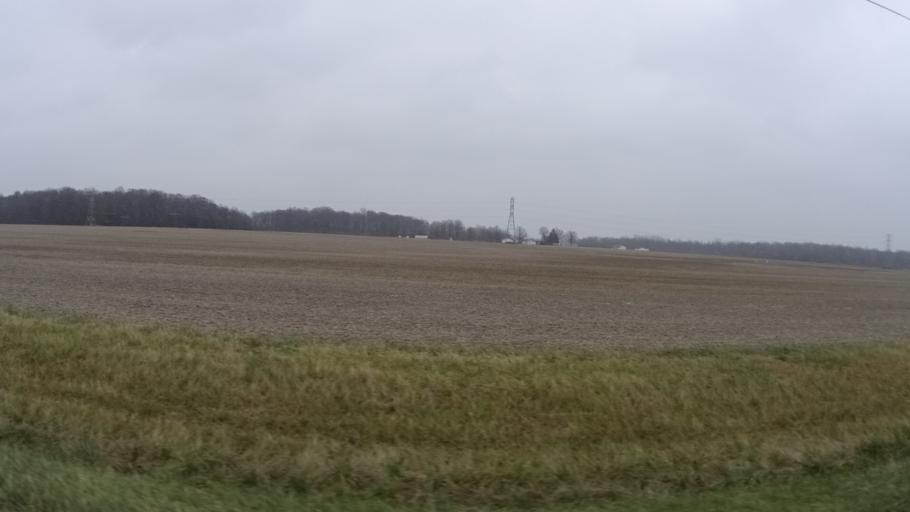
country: US
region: Ohio
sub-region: Lorain County
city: Oberlin
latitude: 41.2927
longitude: -82.2743
